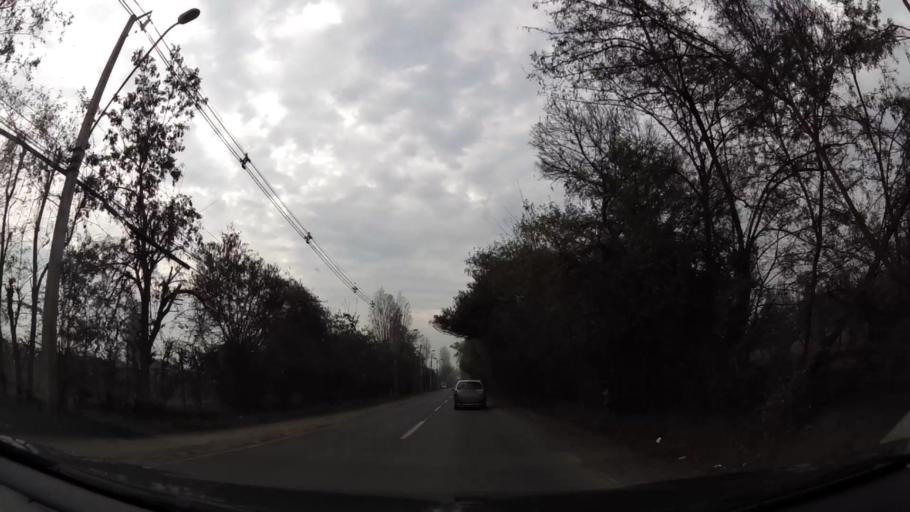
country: CL
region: Santiago Metropolitan
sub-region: Provincia de Chacabuco
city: Chicureo Abajo
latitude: -33.2396
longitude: -70.7488
